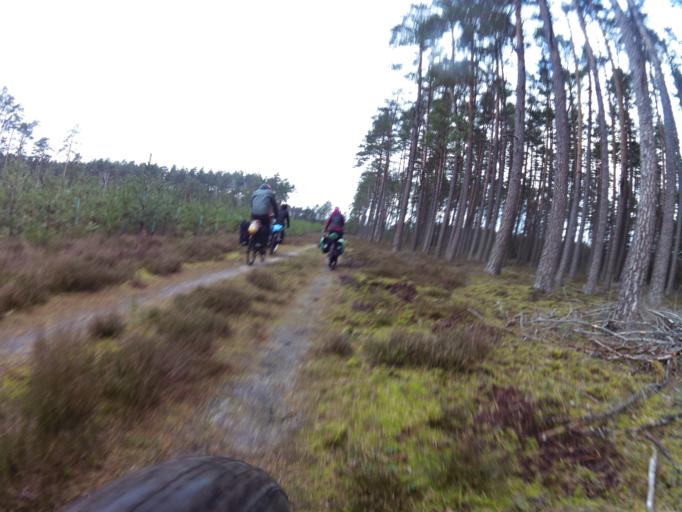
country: PL
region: Pomeranian Voivodeship
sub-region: Powiat slupski
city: Kepice
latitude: 54.3116
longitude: 16.8246
